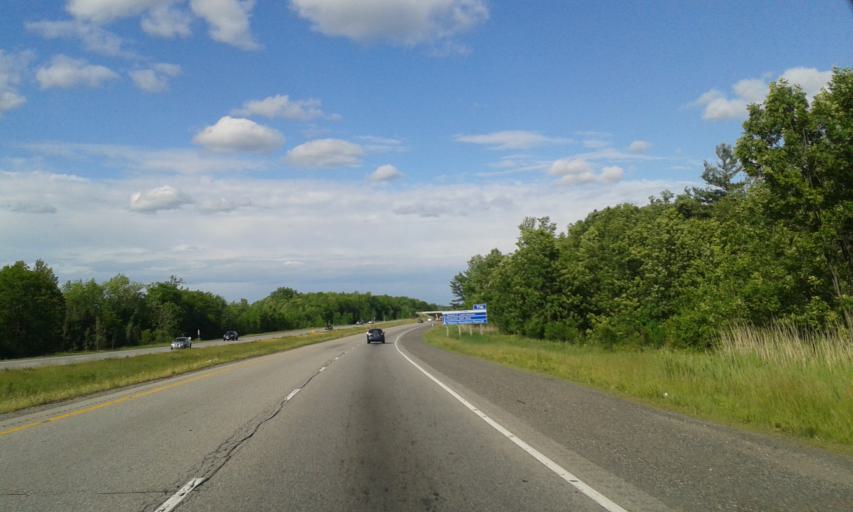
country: CA
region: Ontario
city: Prescott
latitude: 44.7140
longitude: -75.5515
